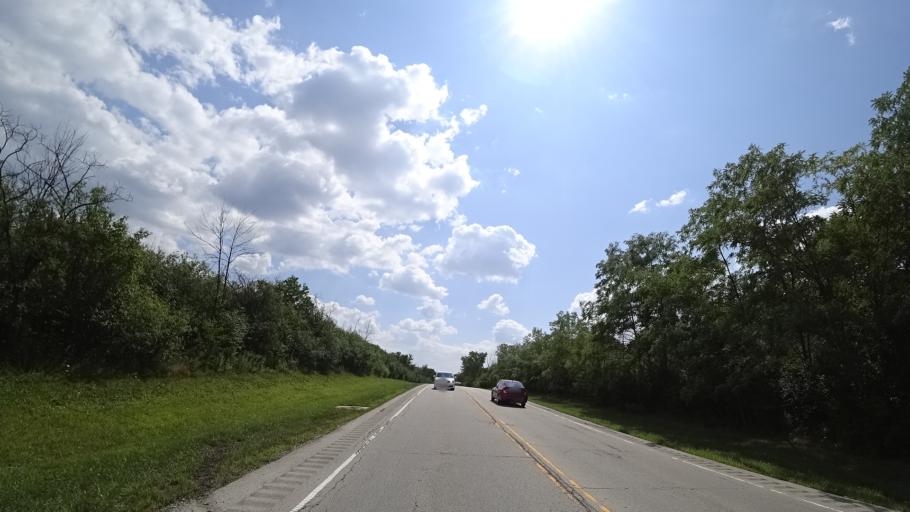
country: US
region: Illinois
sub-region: Cook County
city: Oak Forest
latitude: 41.6205
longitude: -87.7859
